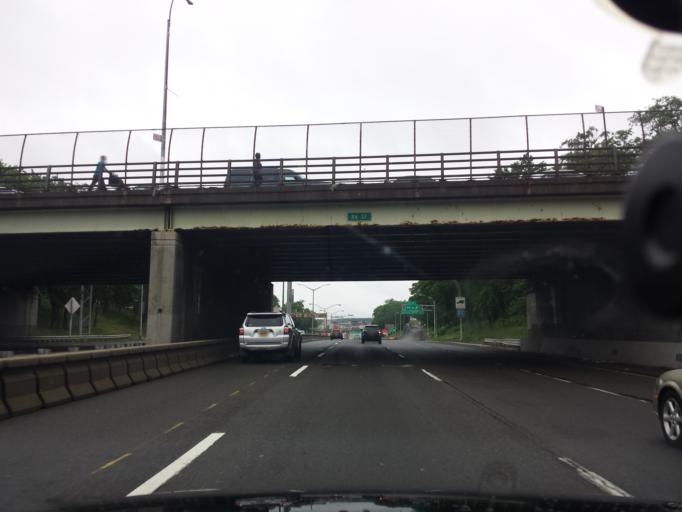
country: US
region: New York
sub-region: Kings County
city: Bensonhurst
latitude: 40.6199
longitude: -74.0232
